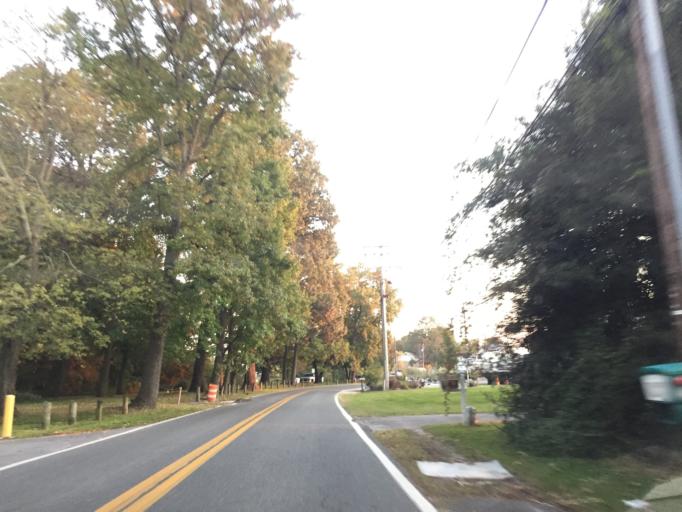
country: US
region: Maryland
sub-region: Baltimore County
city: Essex
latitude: 39.2978
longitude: -76.4663
